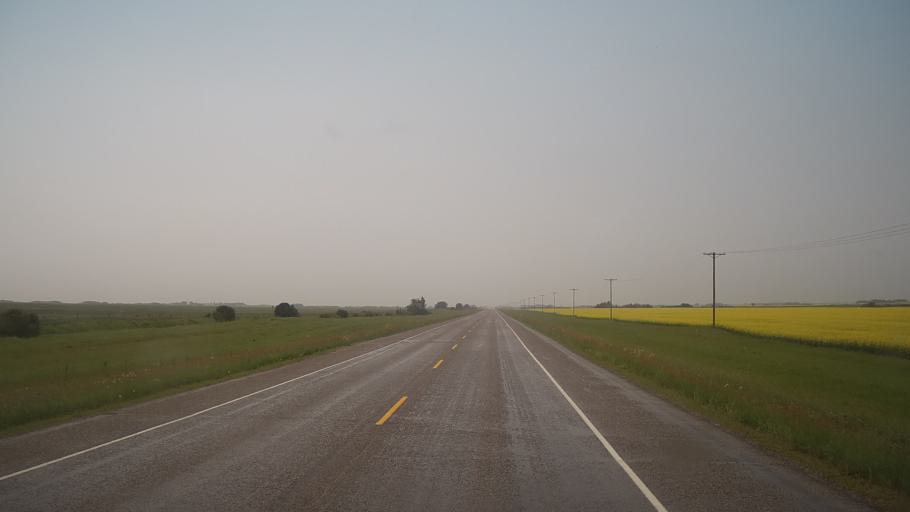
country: CA
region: Saskatchewan
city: Biggar
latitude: 52.1481
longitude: -108.2195
